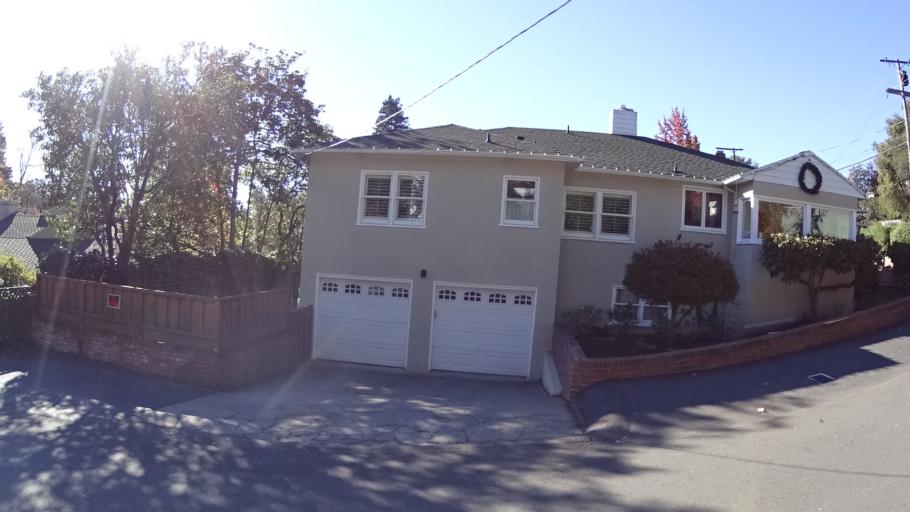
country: US
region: California
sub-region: Alameda County
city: Piedmont
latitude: 37.8331
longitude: -122.2214
